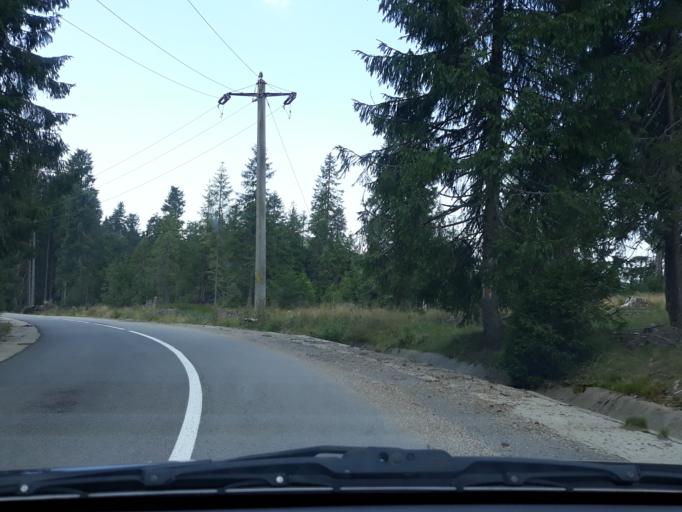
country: RO
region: Alba
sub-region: Comuna Arieseni
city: Arieseni
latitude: 46.5970
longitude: 22.7289
